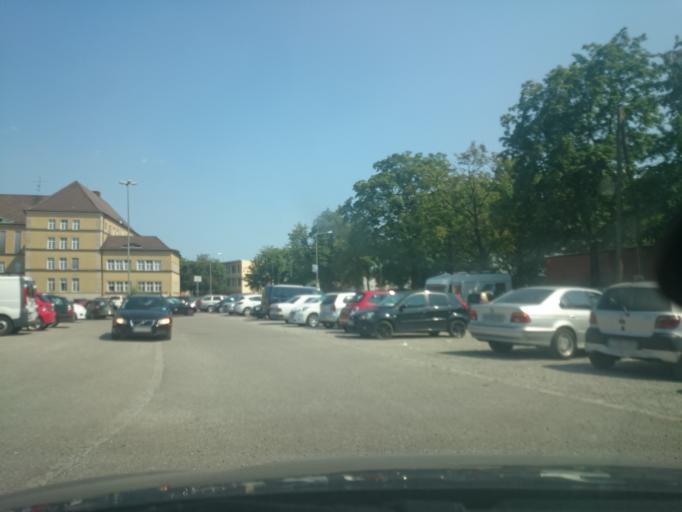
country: DE
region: Bavaria
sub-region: Swabia
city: Augsburg
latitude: 48.3745
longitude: 10.8814
